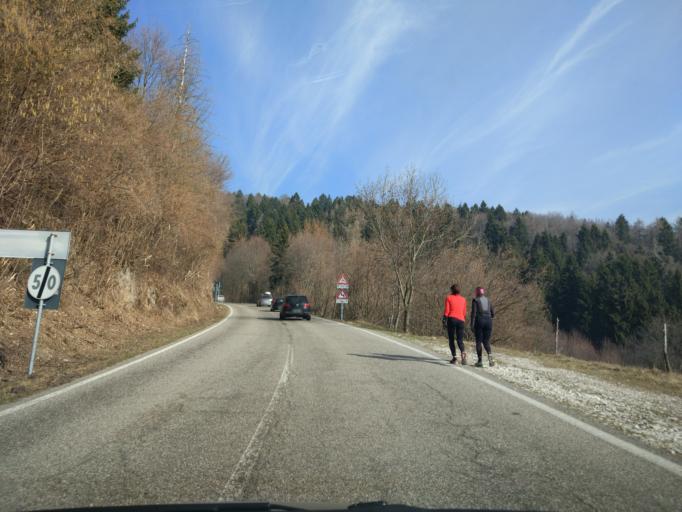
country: IT
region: Veneto
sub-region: Provincia di Verona
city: Bosco Chiesanuova
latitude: 45.6244
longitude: 11.0362
